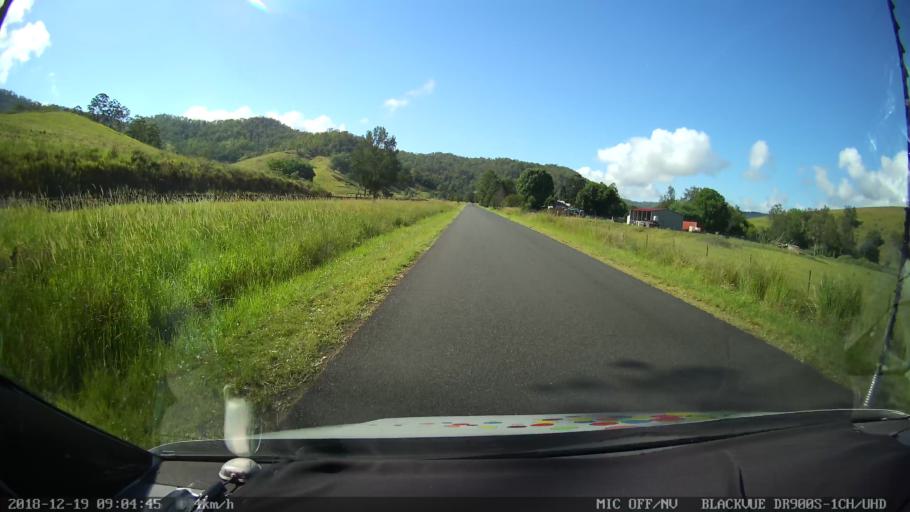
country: AU
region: New South Wales
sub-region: Kyogle
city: Kyogle
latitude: -28.4574
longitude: 152.9443
